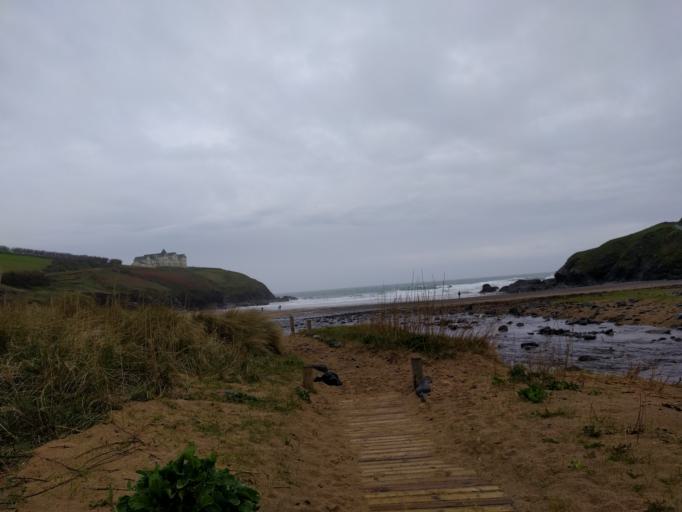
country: GB
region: England
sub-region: Cornwall
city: Mullion
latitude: 50.0345
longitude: -5.2602
